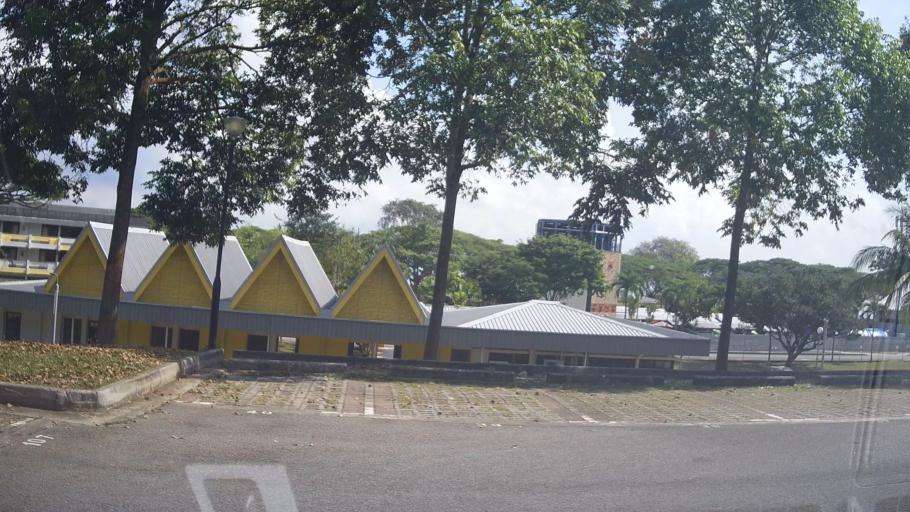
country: MY
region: Johor
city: Kampung Pasir Gudang Baru
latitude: 1.3846
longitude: 103.9424
